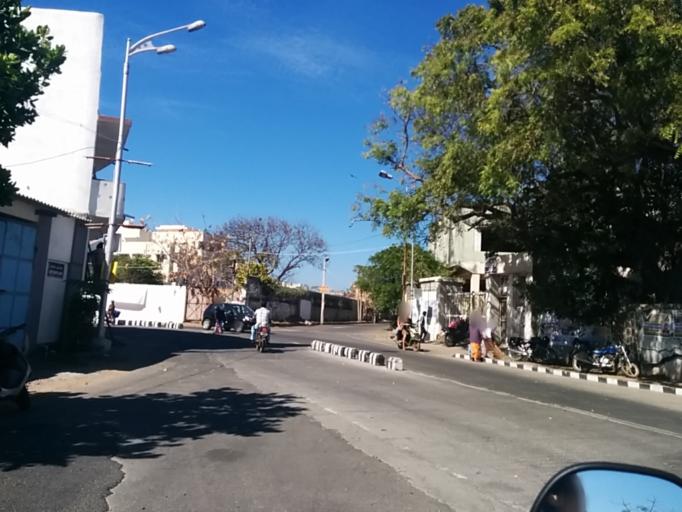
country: IN
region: Pondicherry
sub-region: Puducherry
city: Puducherry
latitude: 11.9387
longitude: 79.8360
